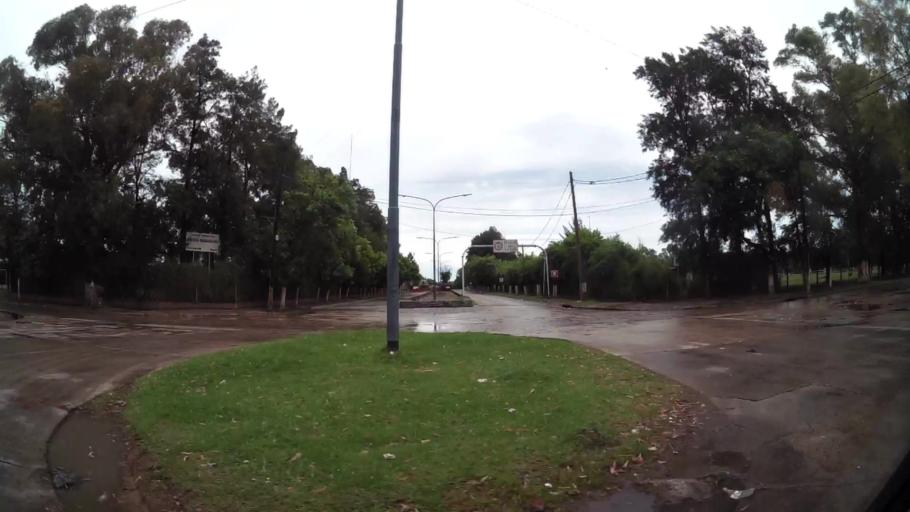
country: AR
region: Buenos Aires F.D.
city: Villa Lugano
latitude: -34.6567
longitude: -58.4464
